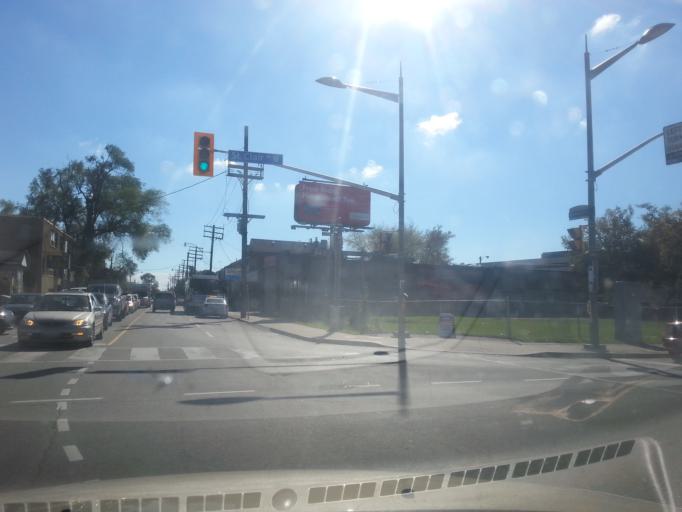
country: CA
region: Ontario
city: Toronto
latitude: 43.6736
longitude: -79.4631
